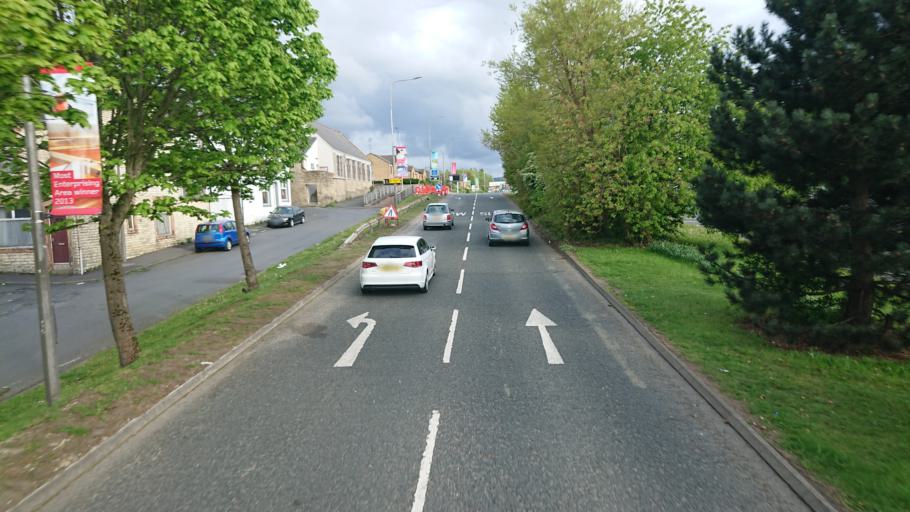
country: GB
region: England
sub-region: Lancashire
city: Burnley
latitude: 53.7967
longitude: -2.2500
